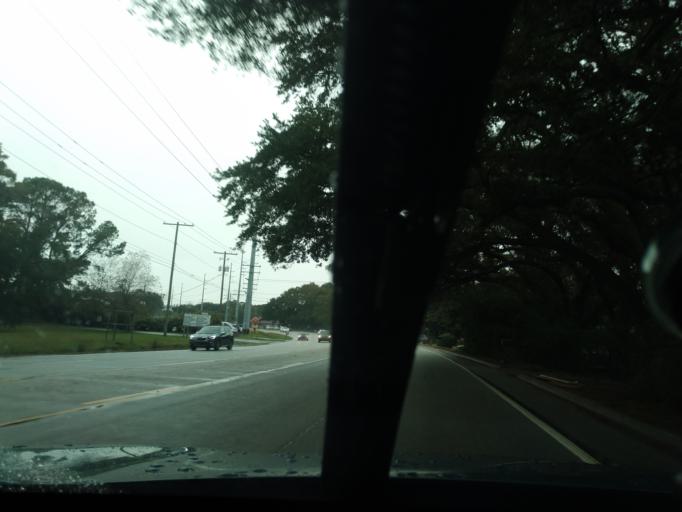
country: US
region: South Carolina
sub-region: Charleston County
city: Folly Beach
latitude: 32.7073
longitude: -79.9641
